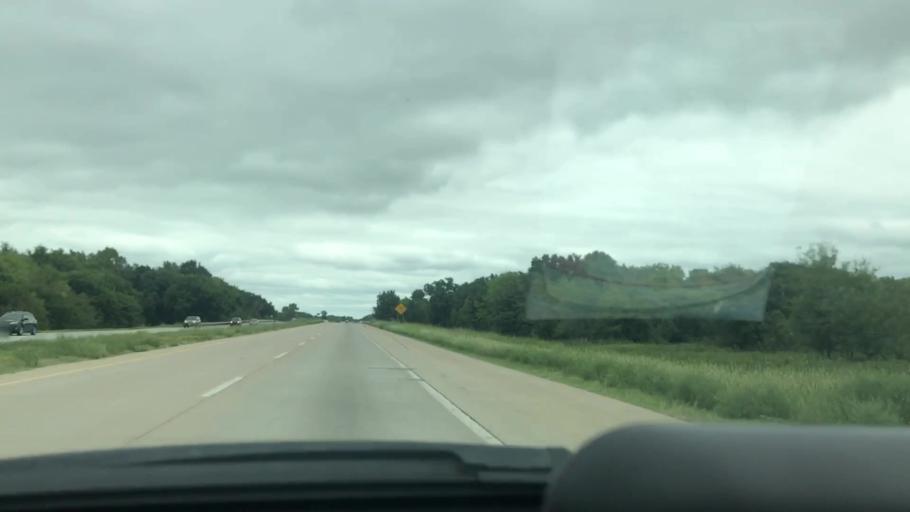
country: US
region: Oklahoma
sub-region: Mayes County
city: Chouteau
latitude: 36.2043
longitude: -95.3408
